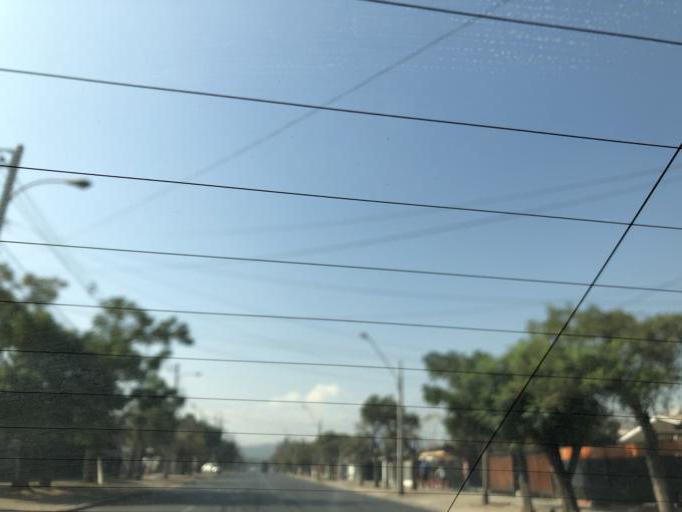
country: CL
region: Santiago Metropolitan
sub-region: Provincia de Cordillera
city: Puente Alto
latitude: -33.6053
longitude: -70.5701
